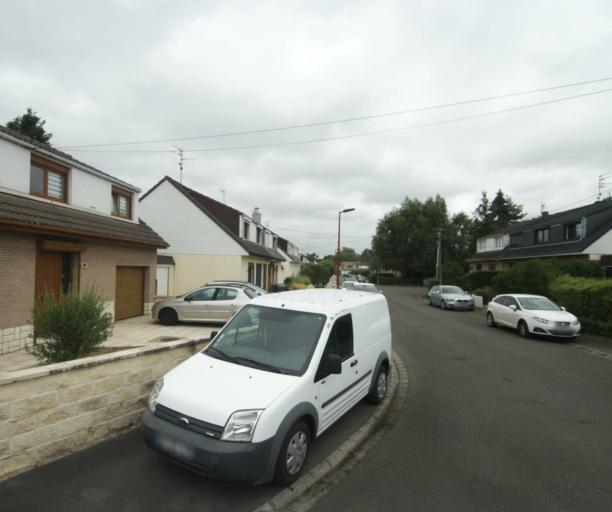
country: FR
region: Nord-Pas-de-Calais
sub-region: Departement du Nord
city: Leers
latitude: 50.6851
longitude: 3.2536
